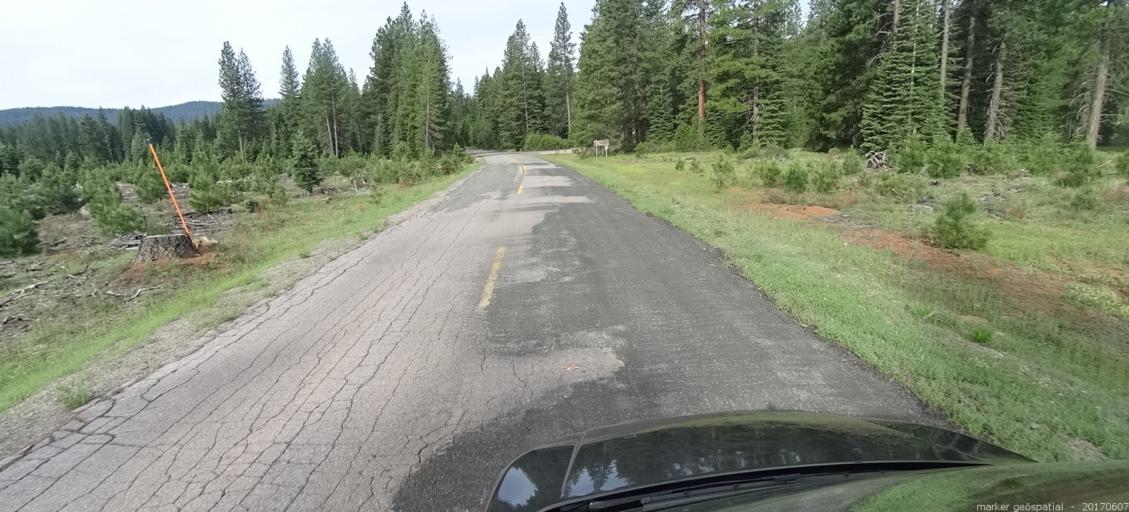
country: US
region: California
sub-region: Shasta County
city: Burney
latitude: 41.1932
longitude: -121.6970
